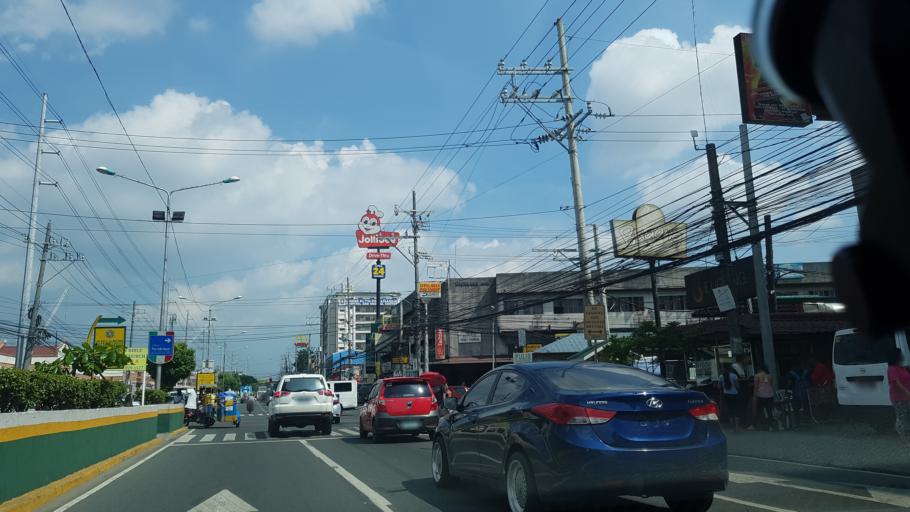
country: PH
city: Sambayanihan People's Village
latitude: 14.4658
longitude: 121.0174
